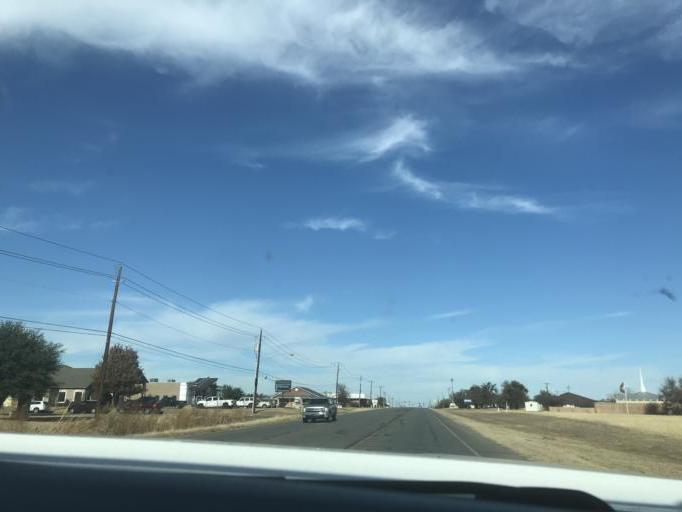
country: US
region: Texas
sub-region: Erath County
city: Stephenville
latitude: 32.2167
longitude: -98.2404
